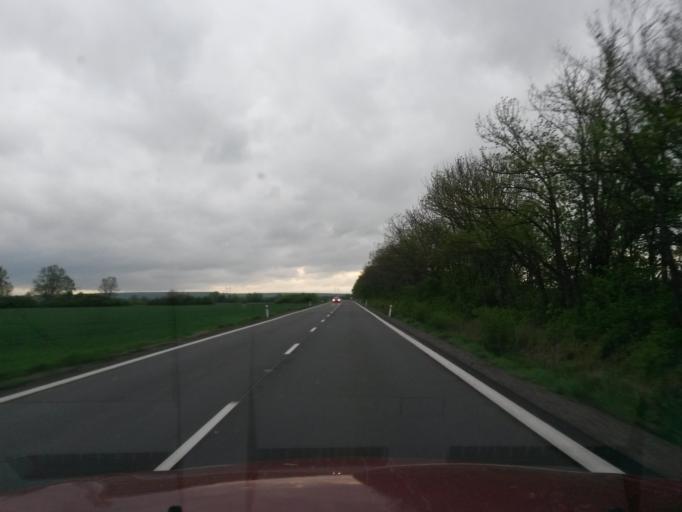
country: SK
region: Kosicky
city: Secovce
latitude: 48.6998
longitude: 21.7322
